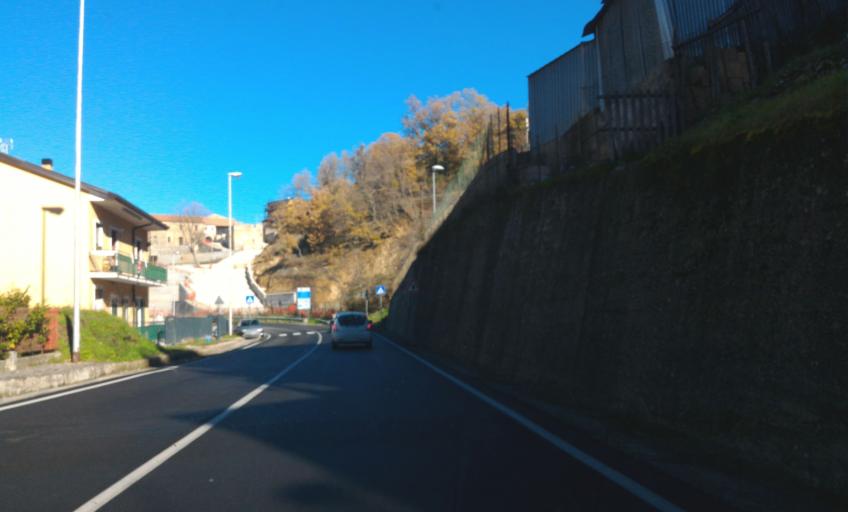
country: IT
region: Calabria
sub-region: Provincia di Cosenza
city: Spezzano della Sila
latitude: 39.2988
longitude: 16.3422
